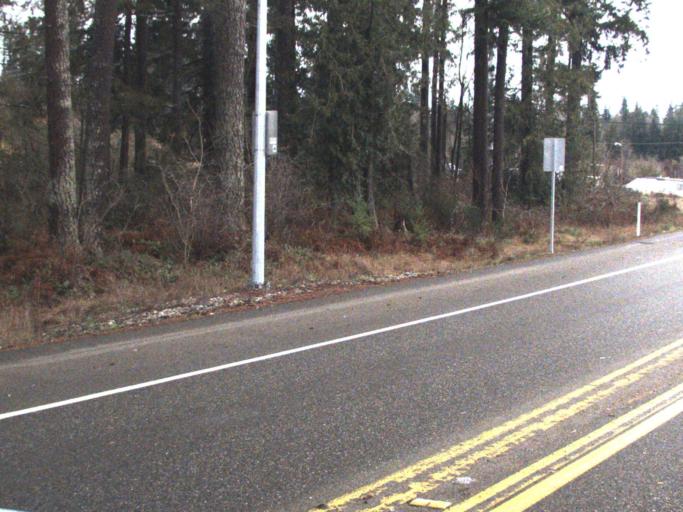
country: US
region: Washington
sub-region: Snohomish County
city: Granite Falls
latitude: 48.0869
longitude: -121.9906
